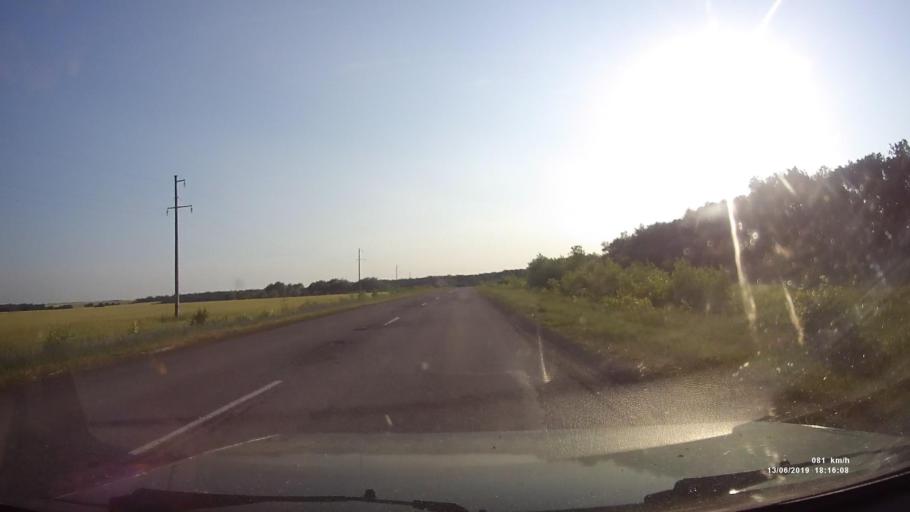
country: RU
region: Rostov
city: Kazanskaya
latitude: 49.9282
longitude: 41.3444
